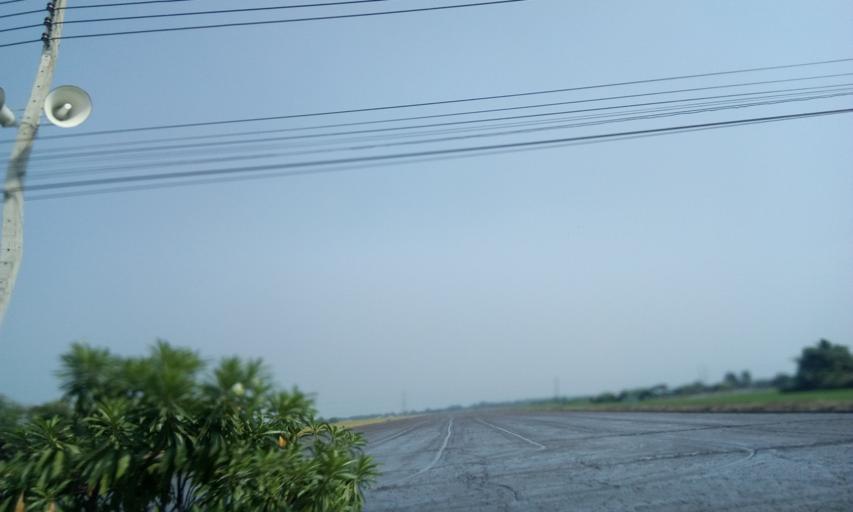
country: TH
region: Pathum Thani
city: Ban Rangsit
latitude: 13.9987
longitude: 100.7567
